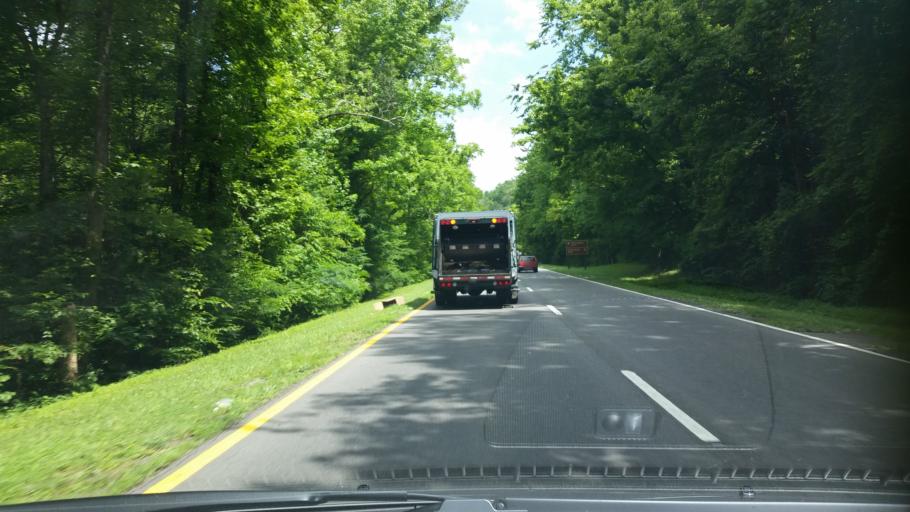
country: US
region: Tennessee
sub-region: Sevier County
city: Gatlinburg
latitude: 35.7302
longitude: -83.5191
